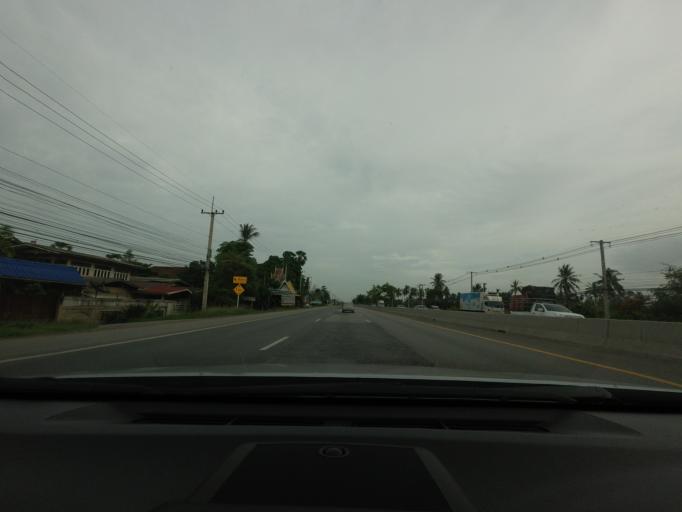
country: TH
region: Phetchaburi
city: Tha Yang
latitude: 12.9320
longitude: 99.9051
